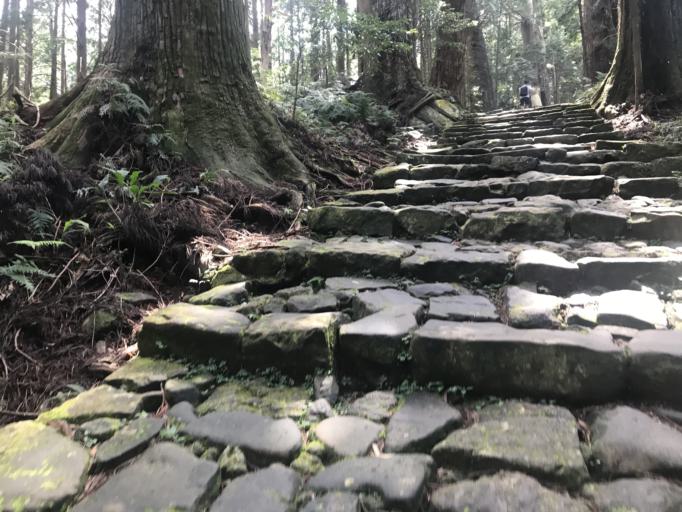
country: JP
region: Wakayama
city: Shingu
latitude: 33.6702
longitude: 135.8959
